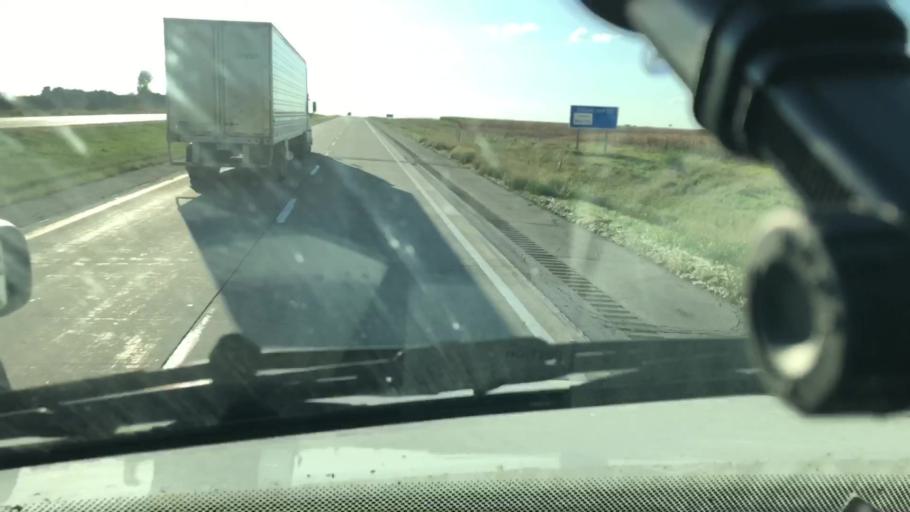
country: US
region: Iowa
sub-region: Pottawattamie County
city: Avoca
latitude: 41.4996
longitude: -95.5038
